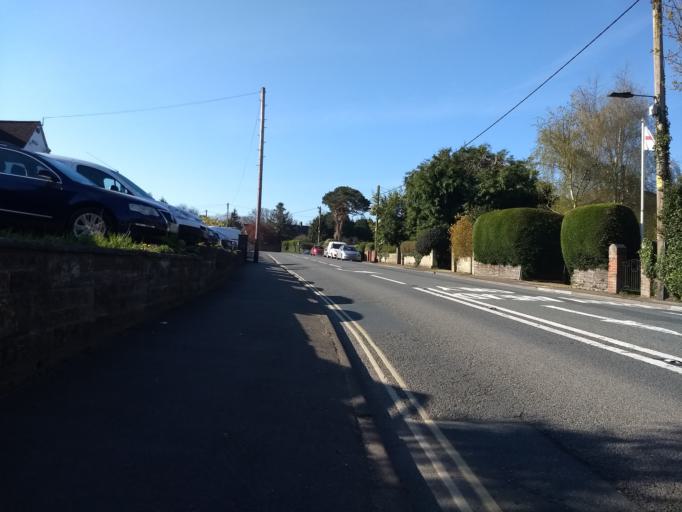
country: GB
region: England
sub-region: Isle of Wight
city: Ryde
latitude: 50.7299
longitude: -1.2155
